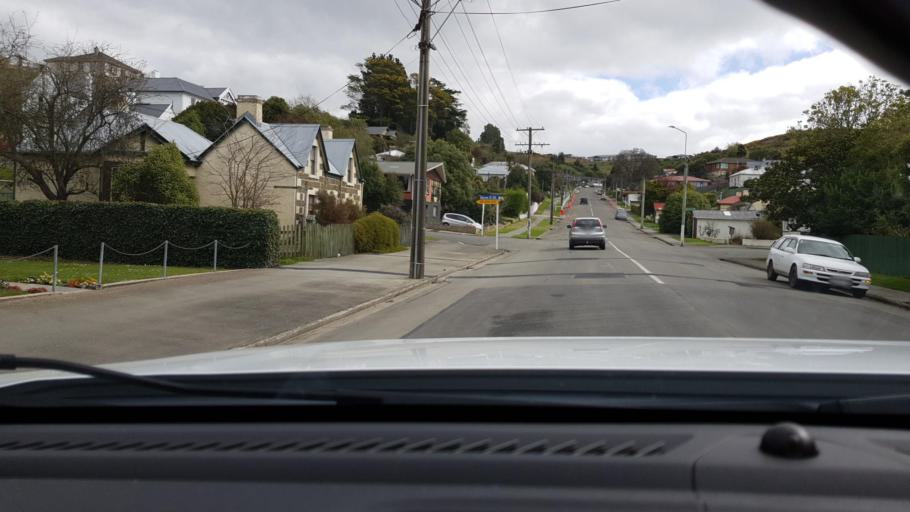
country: NZ
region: Otago
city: Oamaru
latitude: -45.0953
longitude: 170.9664
